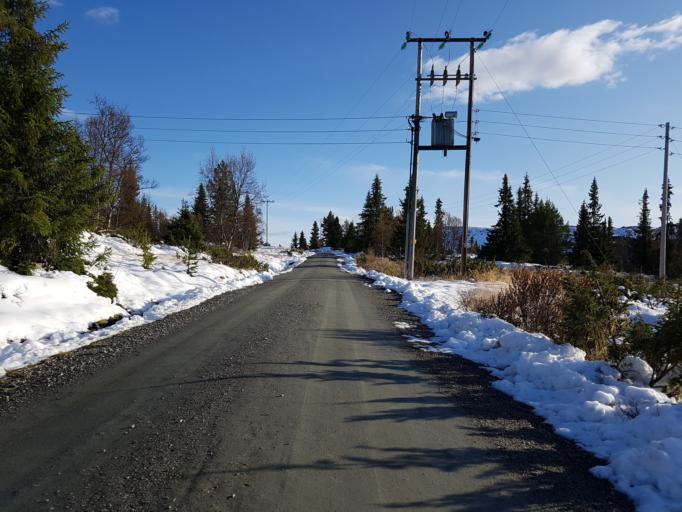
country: NO
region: Oppland
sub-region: Sel
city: Otta
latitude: 61.8167
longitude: 9.6778
